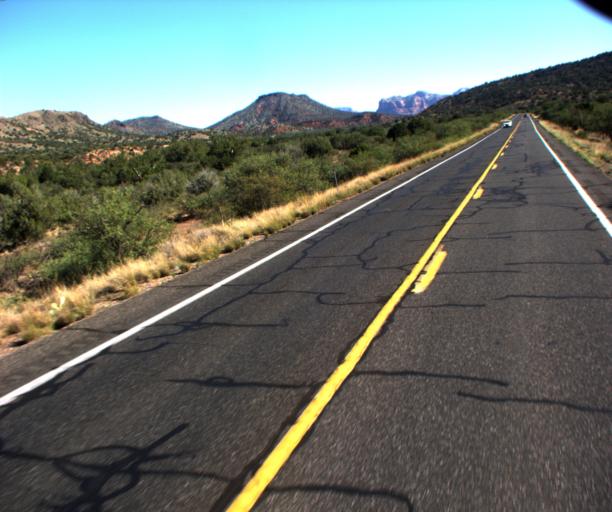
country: US
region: Arizona
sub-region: Yavapai County
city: Big Park
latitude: 34.7169
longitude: -111.7777
